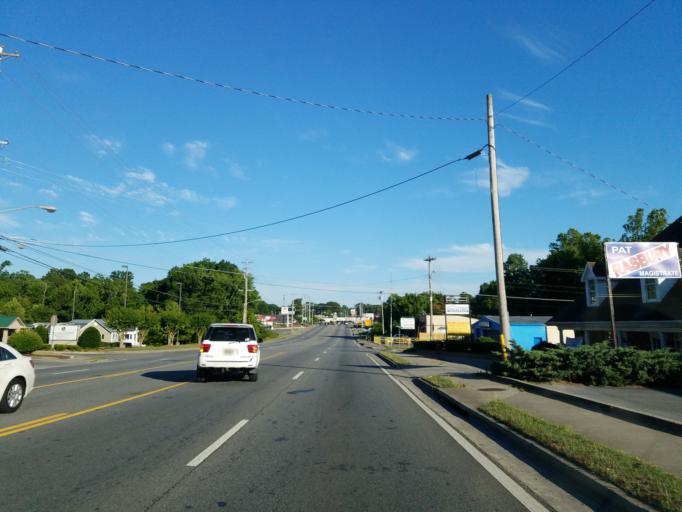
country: US
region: Georgia
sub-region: Gordon County
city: Calhoun
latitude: 34.4887
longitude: -84.9465
